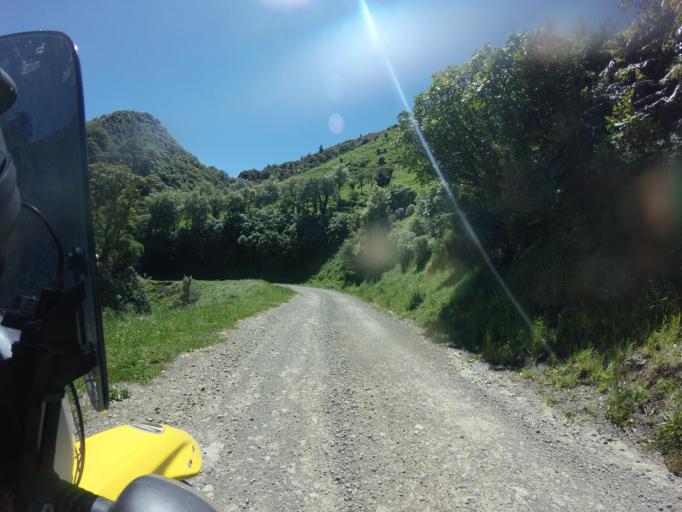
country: NZ
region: Bay of Plenty
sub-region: Opotiki District
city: Opotiki
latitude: -38.4130
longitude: 177.3956
